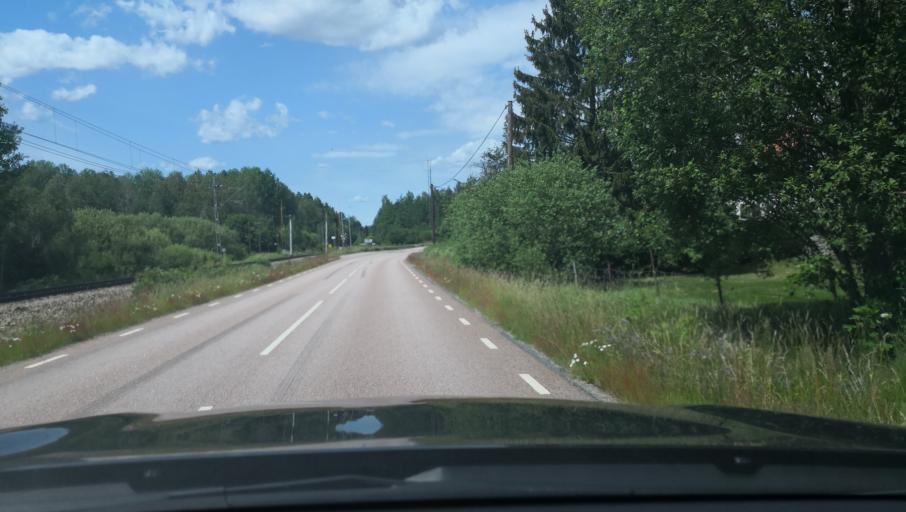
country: SE
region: Vaestmanland
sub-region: Surahammars Kommun
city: Ramnas
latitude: 59.8219
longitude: 16.1496
